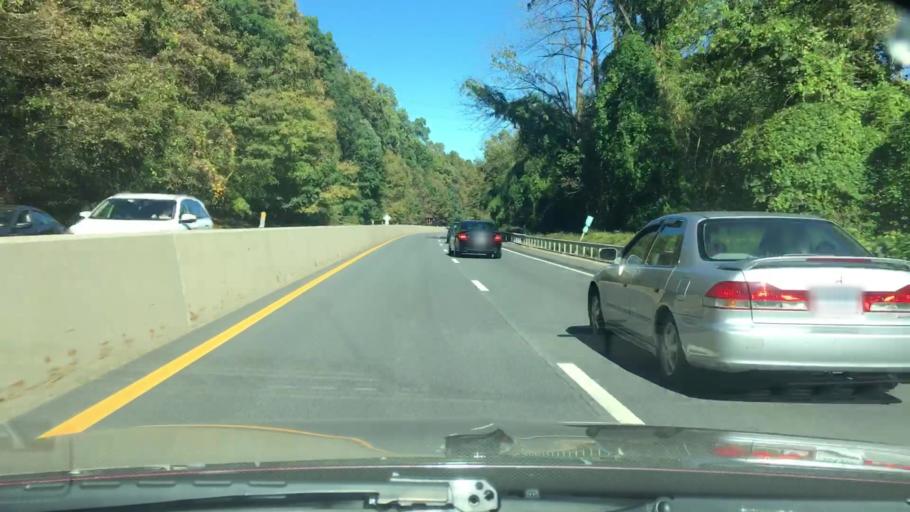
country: US
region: New York
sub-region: Westchester County
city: Pleasantville
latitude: 41.1430
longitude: -73.7903
